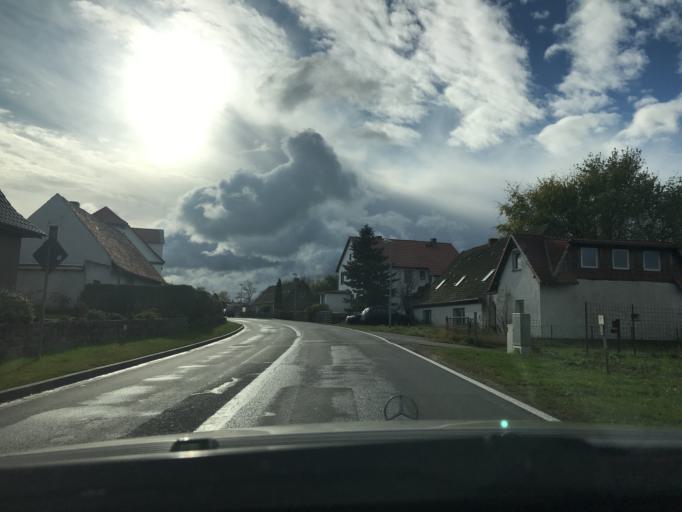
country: DE
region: Mecklenburg-Vorpommern
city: Jarmen
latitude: 53.8805
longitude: 13.3356
